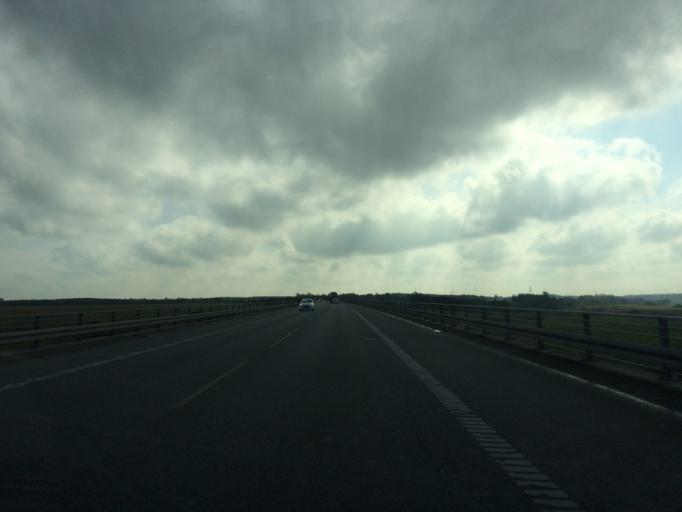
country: DK
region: Central Jutland
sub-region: Skive Kommune
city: Skive
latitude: 56.5464
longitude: 8.9947
